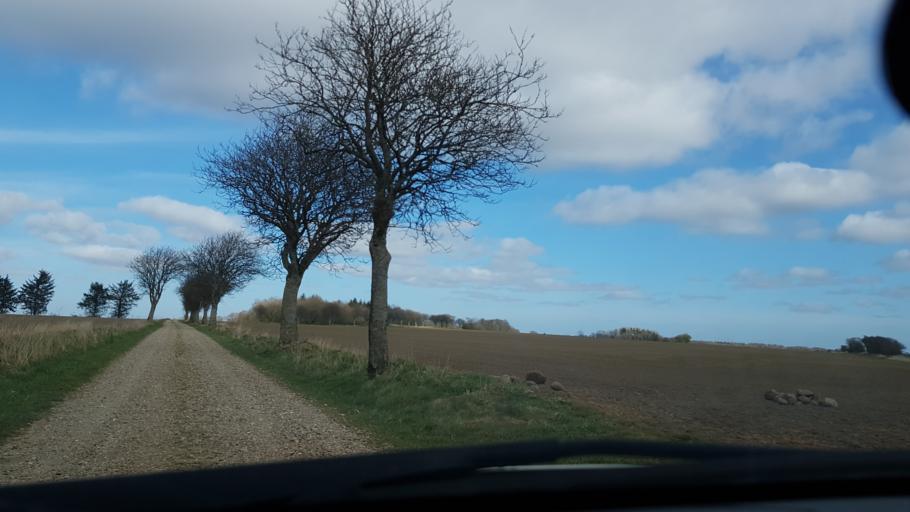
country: DK
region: South Denmark
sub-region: Vejen Kommune
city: Brorup
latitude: 55.4247
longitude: 9.0261
